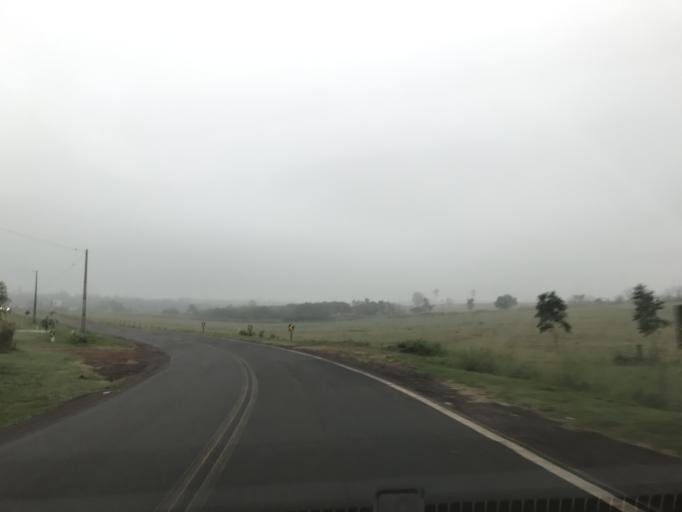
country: PY
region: Canindeyu
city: Salto del Guaira
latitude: -24.0864
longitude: -54.0909
